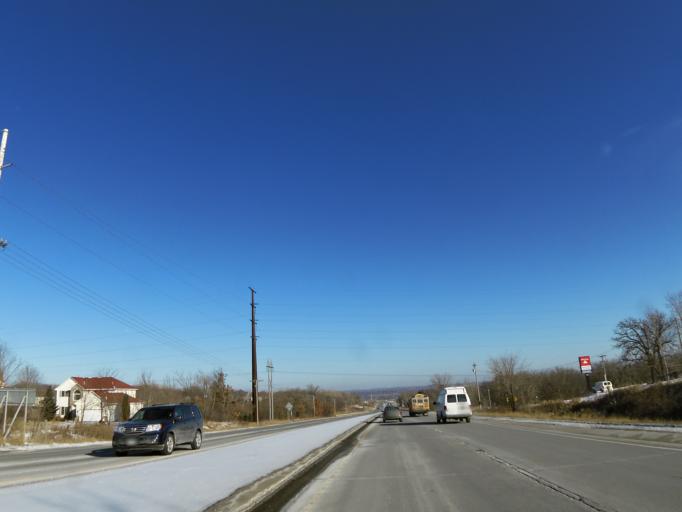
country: US
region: Minnesota
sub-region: Scott County
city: Savage
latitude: 44.7519
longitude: -93.3797
